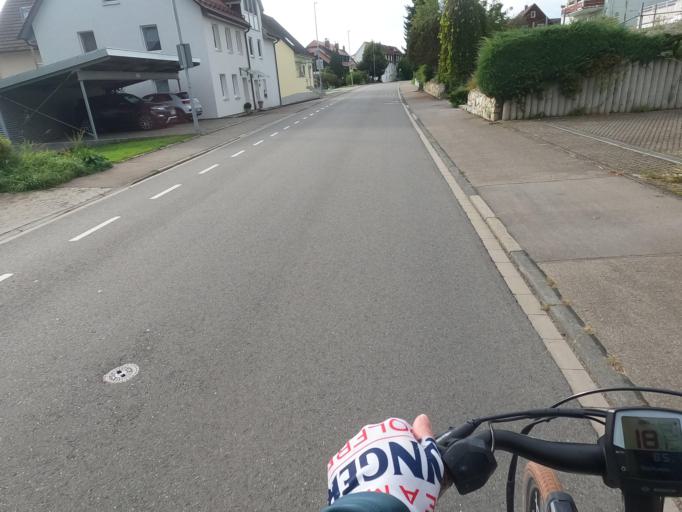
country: DE
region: Baden-Wuerttemberg
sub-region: Freiburg Region
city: Allensbach
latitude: 47.7206
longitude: 9.0532
